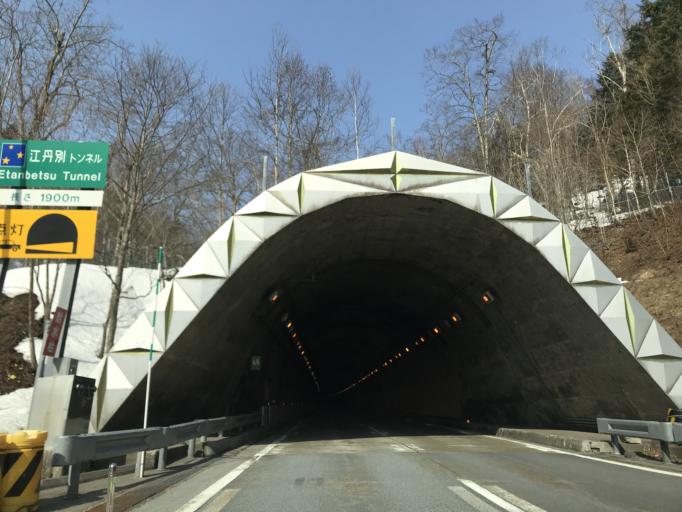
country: JP
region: Hokkaido
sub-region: Asahikawa-shi
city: Asahikawa
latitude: 43.7922
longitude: 142.2642
